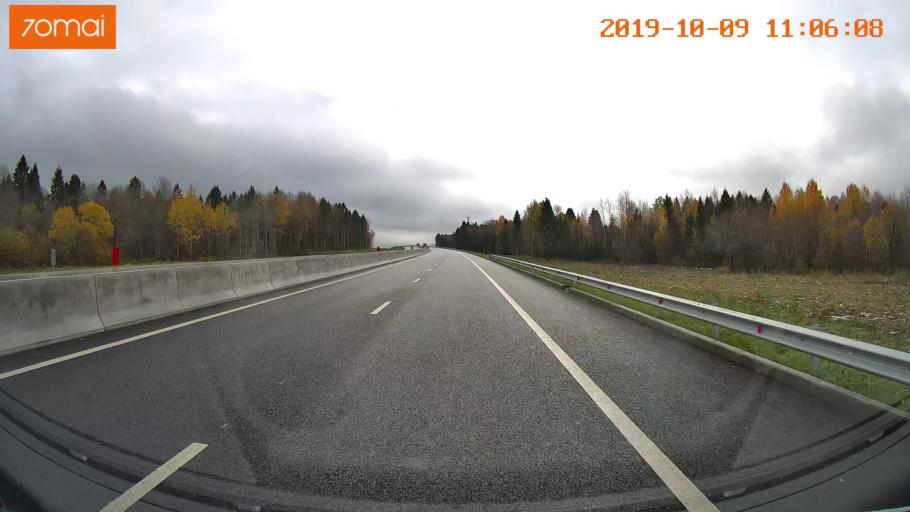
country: RU
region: Vologda
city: Molochnoye
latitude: 59.1905
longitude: 39.7586
